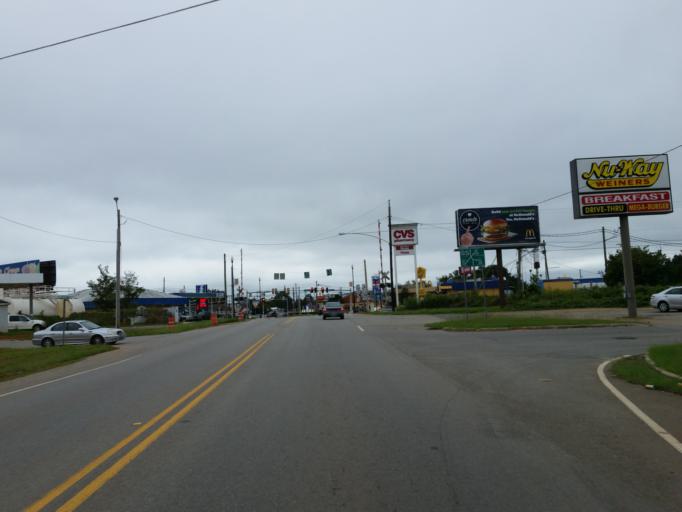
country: US
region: Georgia
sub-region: Peach County
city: Fort Valley
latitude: 32.5604
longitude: -83.8839
